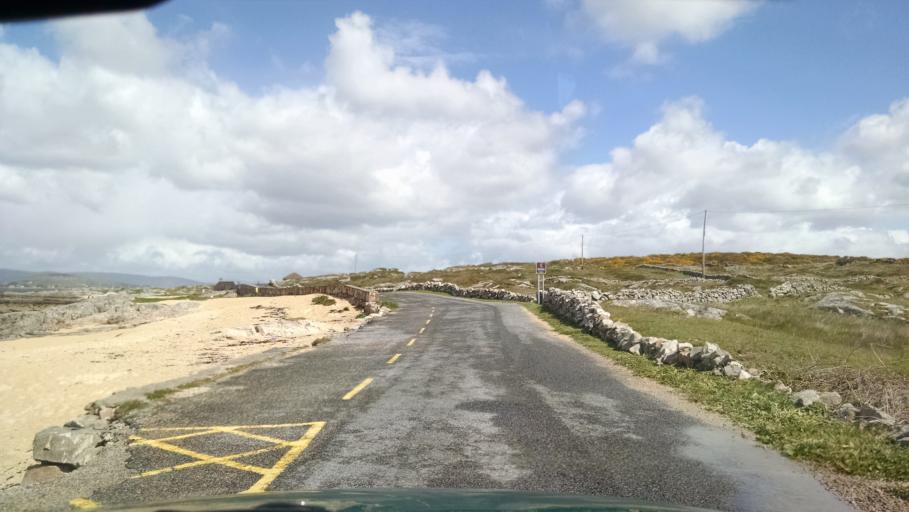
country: IE
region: Connaught
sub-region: County Galway
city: Oughterard
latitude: 53.2470
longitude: -9.6287
